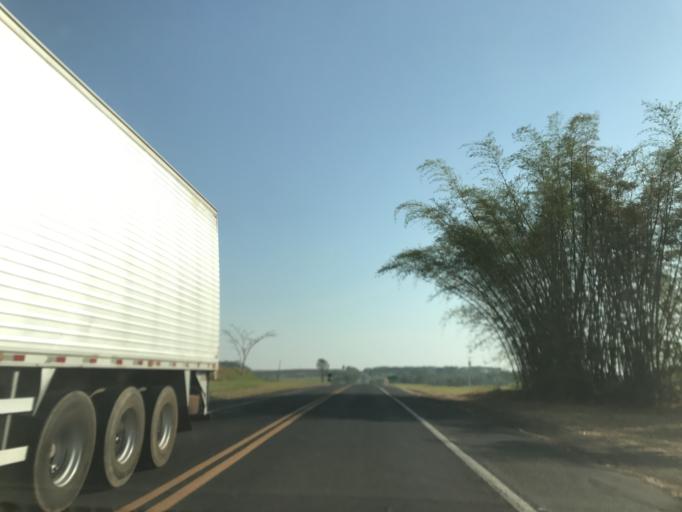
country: BR
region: Sao Paulo
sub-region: Lins
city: Lins
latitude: -21.8956
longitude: -49.9111
